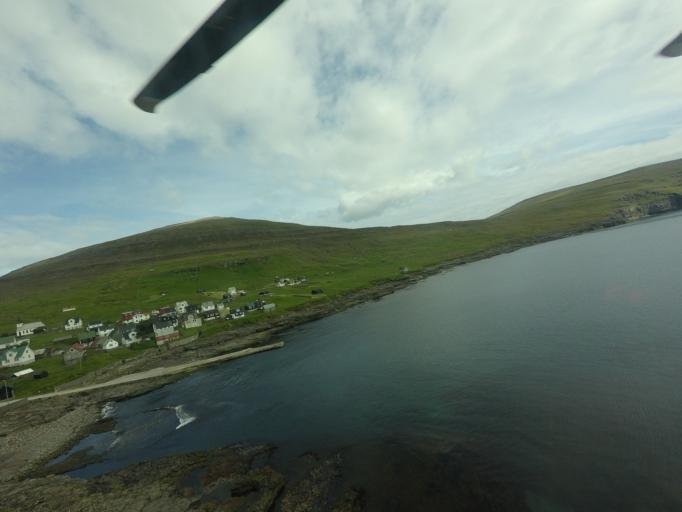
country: FO
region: Nordoyar
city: Klaksvik
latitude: 62.2762
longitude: -6.3394
